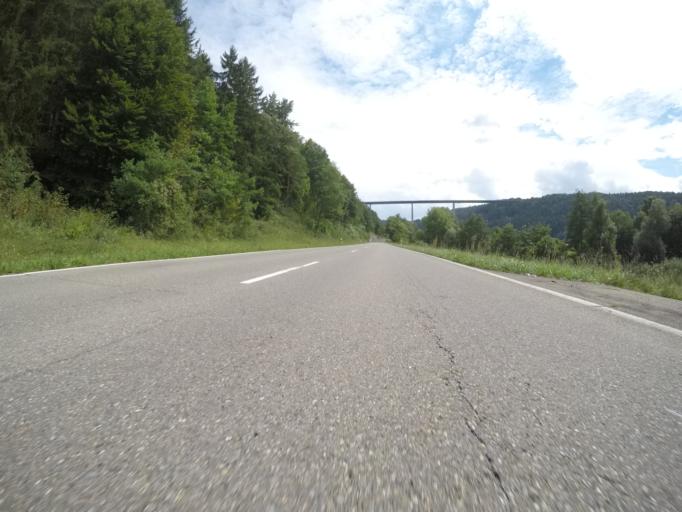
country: DE
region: Baden-Wuerttemberg
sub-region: Karlsruhe Region
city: Horb am Neckar
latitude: 48.4545
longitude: 8.7560
